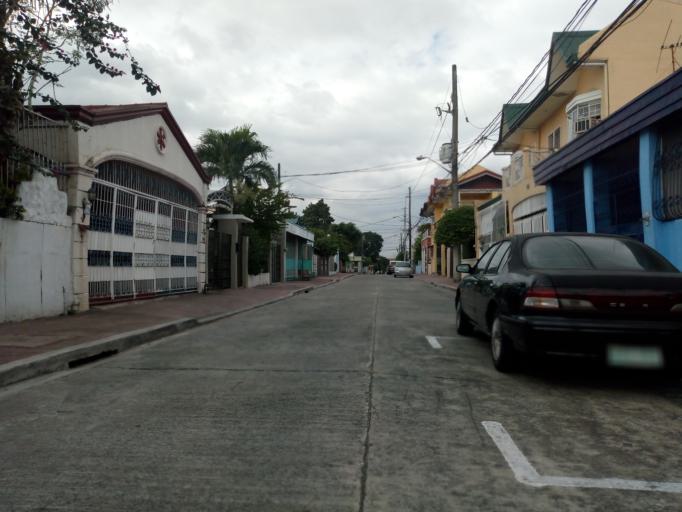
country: PH
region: Calabarzon
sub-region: Province of Rizal
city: Antipolo
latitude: 14.6388
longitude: 121.1200
